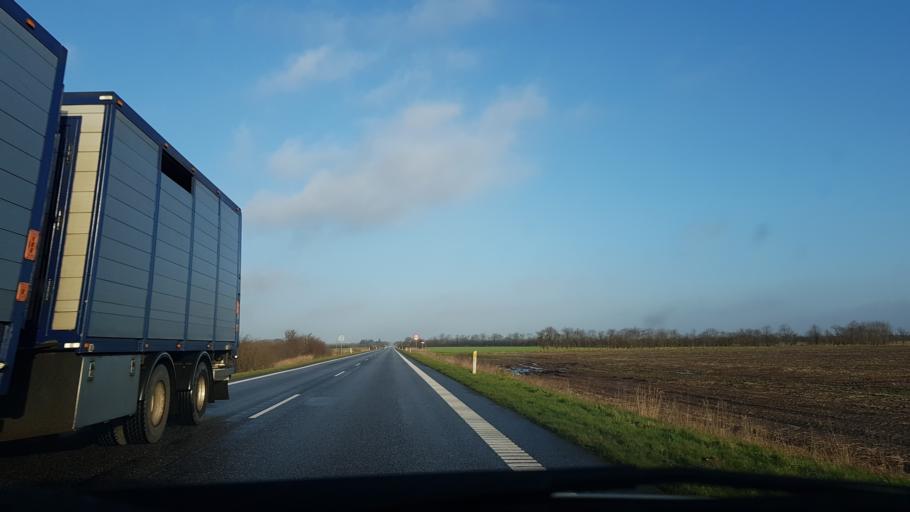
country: DK
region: South Denmark
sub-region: Tonder Kommune
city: Toftlund
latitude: 55.2208
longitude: 9.1078
